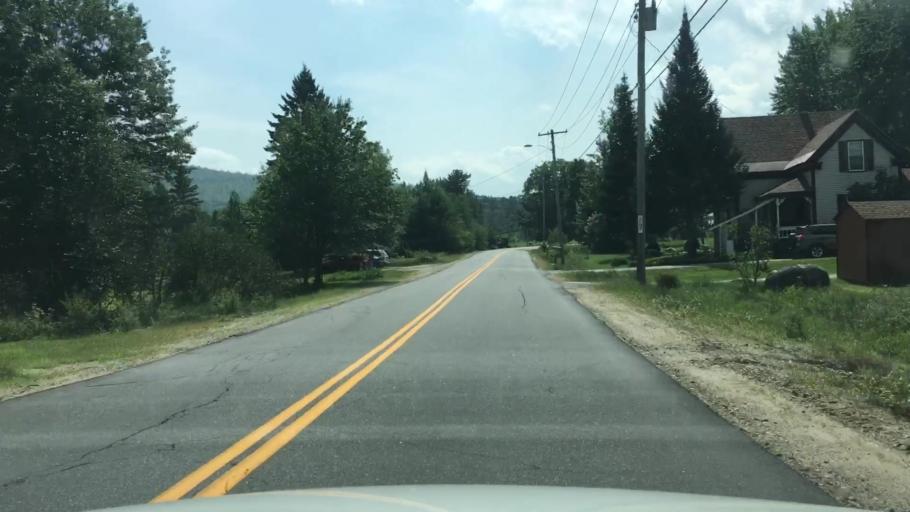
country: US
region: Maine
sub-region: Oxford County
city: Rumford
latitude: 44.5259
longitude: -70.5115
